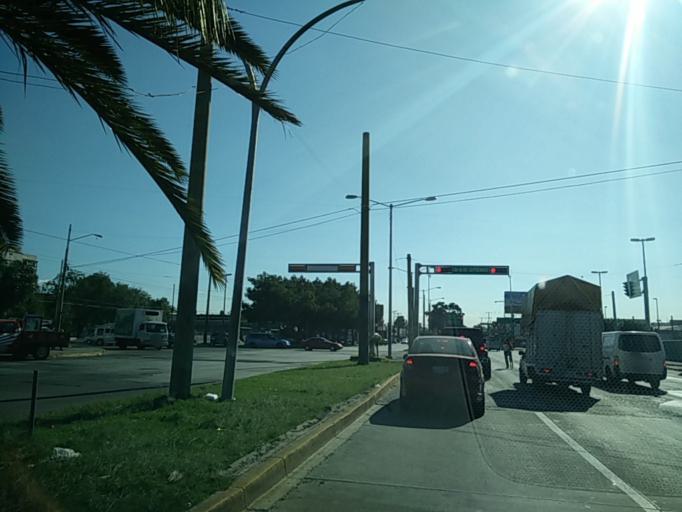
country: MX
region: Jalisco
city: Guadalajara
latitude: 20.6578
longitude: -103.3524
